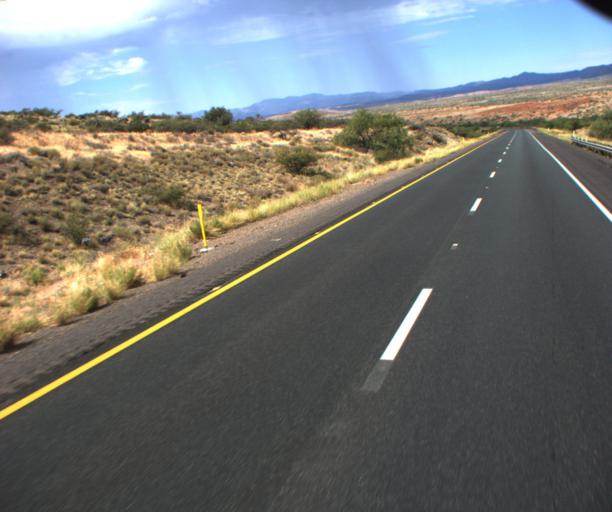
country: US
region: Arizona
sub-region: Yavapai County
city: Cordes Lakes
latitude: 34.4233
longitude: -112.0552
